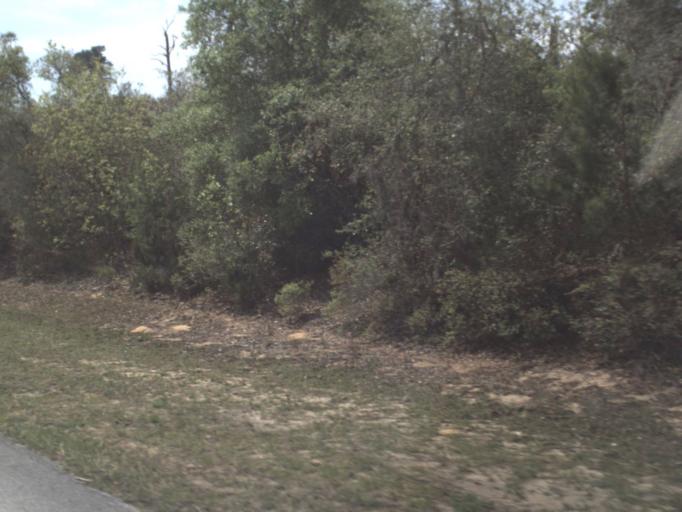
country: US
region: Florida
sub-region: Lake County
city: Astor
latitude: 29.1885
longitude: -81.6550
